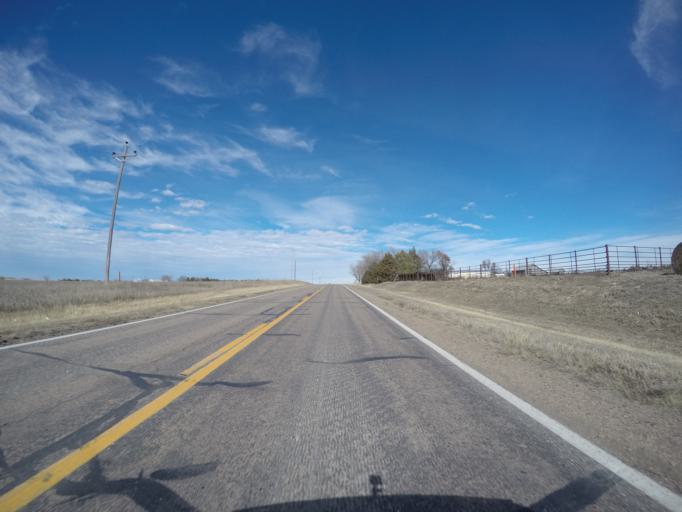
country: US
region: Nebraska
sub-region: Franklin County
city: Franklin
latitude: 40.1647
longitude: -98.9527
